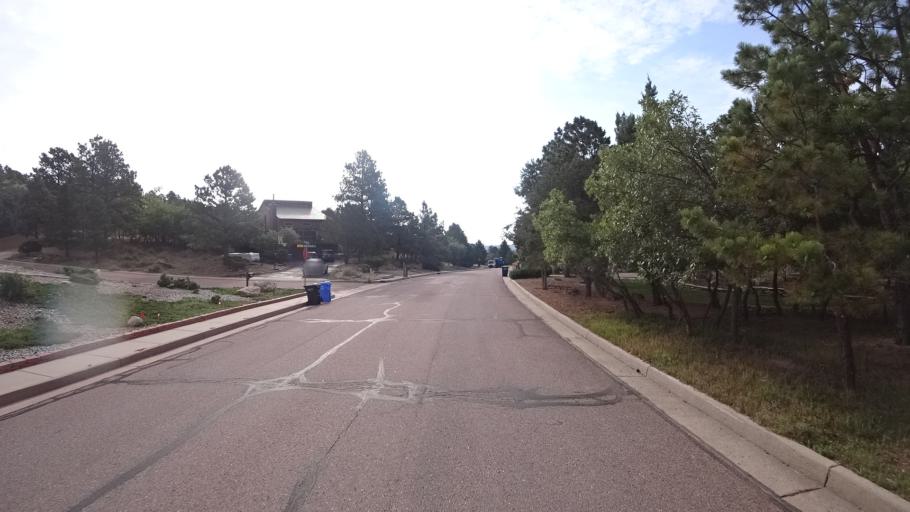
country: US
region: Colorado
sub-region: El Paso County
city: Air Force Academy
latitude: 38.9338
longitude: -104.8497
